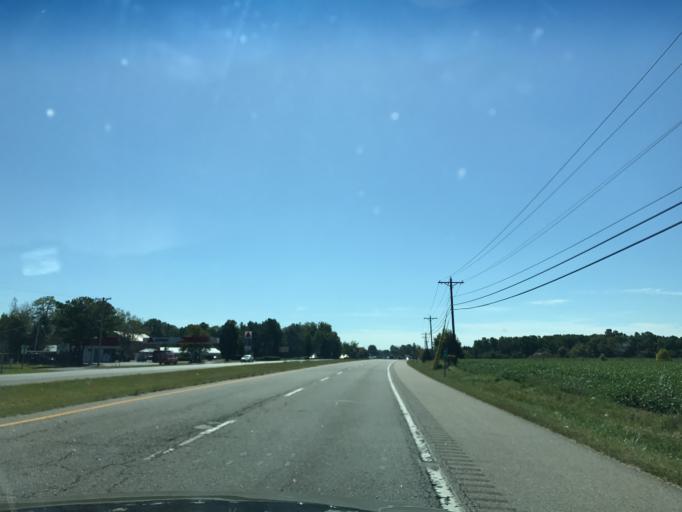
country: US
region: Maryland
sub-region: Charles County
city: La Plata
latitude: 38.4109
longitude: -76.9550
